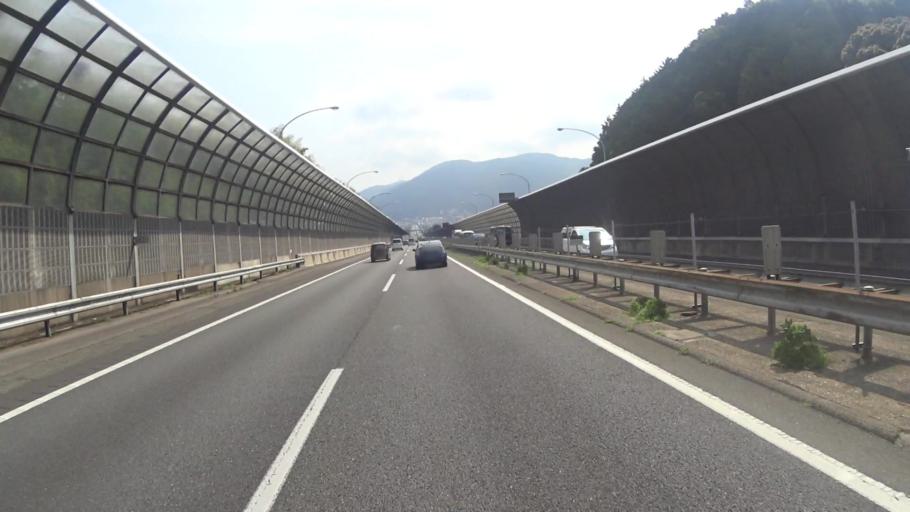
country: JP
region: Kyoto
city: Uji
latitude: 34.9590
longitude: 135.8000
